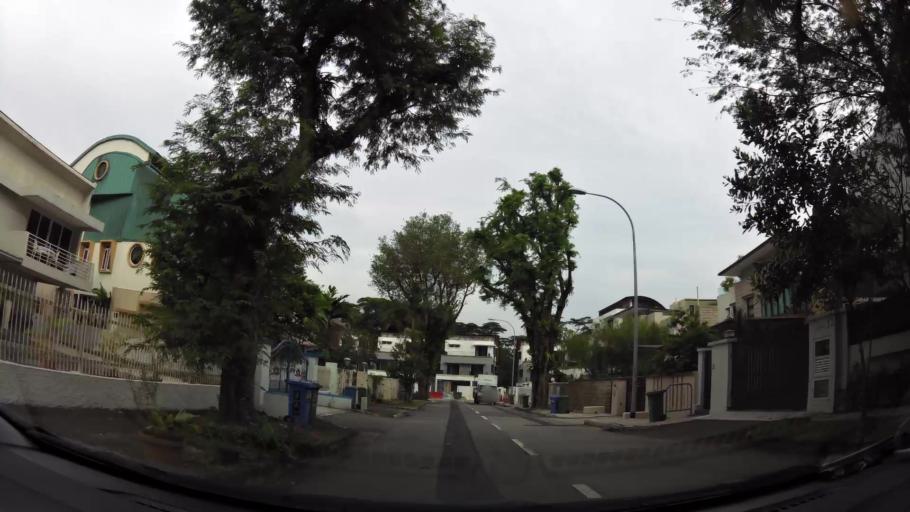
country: MY
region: Johor
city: Kampung Pasir Gudang Baru
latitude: 1.4187
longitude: 103.9089
